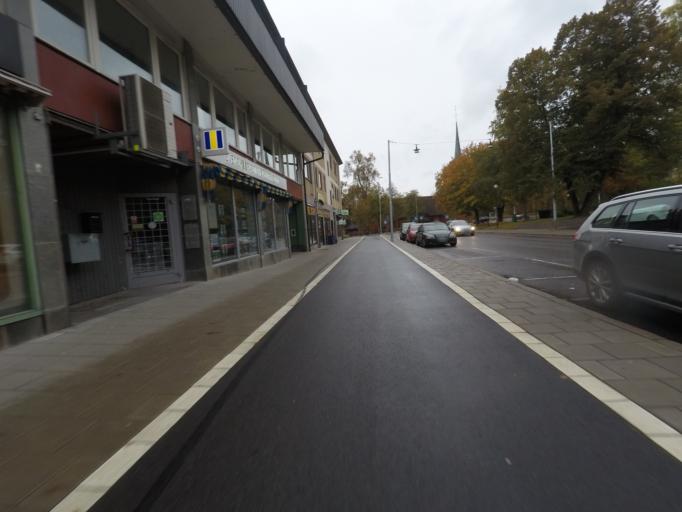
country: SE
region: OErebro
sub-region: Karlskoga Kommun
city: Karlskoga
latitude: 59.3269
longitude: 14.5226
